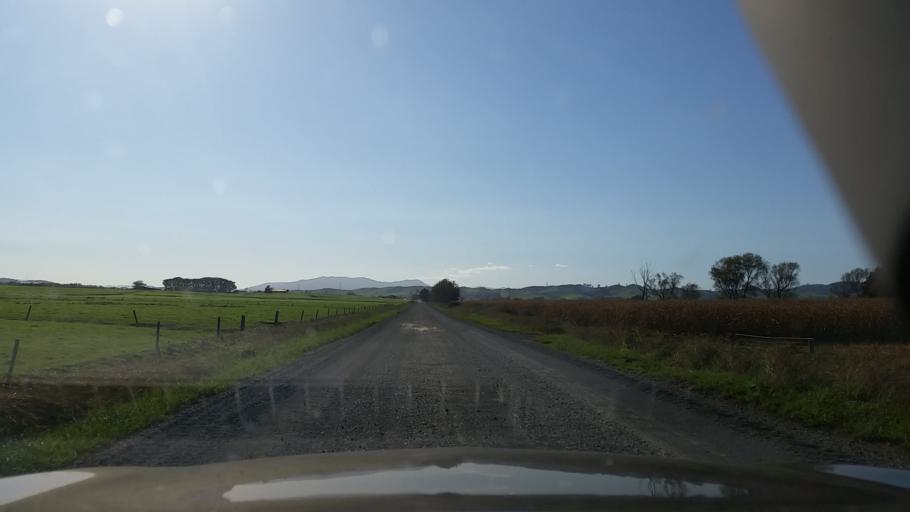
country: NZ
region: Waikato
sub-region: Hamilton City
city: Hamilton
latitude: -37.6319
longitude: 175.4287
